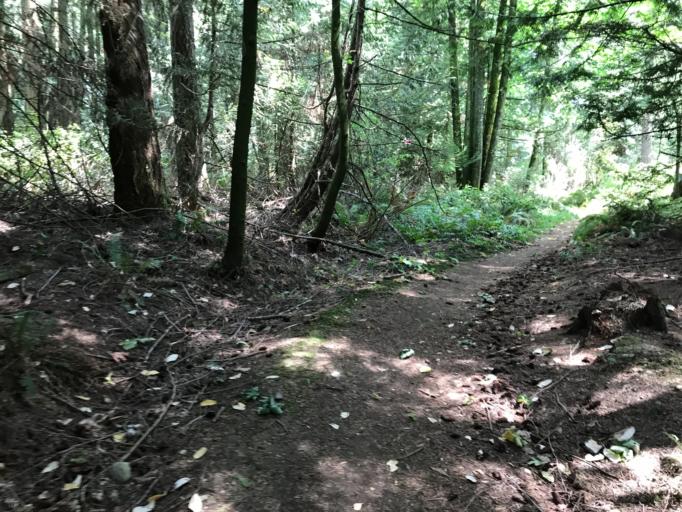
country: CA
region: British Columbia
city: North Cowichan
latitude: 48.9253
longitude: -123.7392
